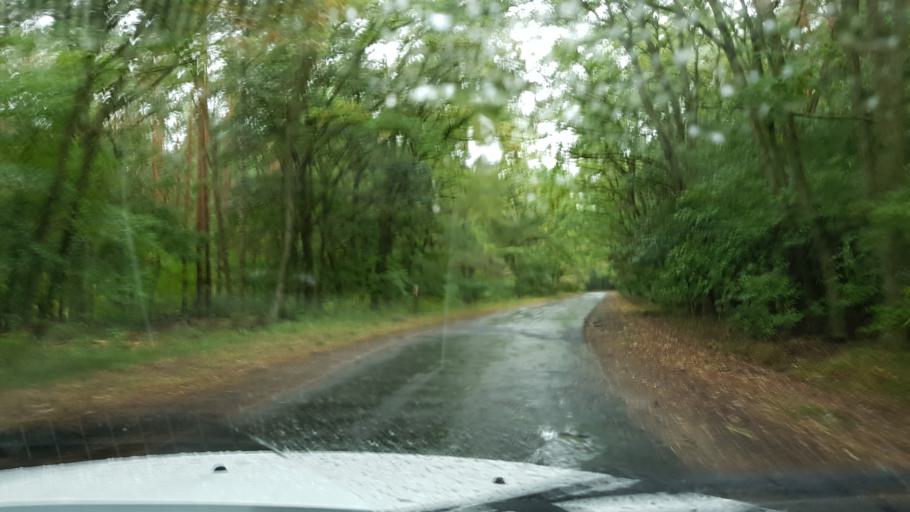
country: DE
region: Brandenburg
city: Meyenburg
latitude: 52.9741
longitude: 14.2330
